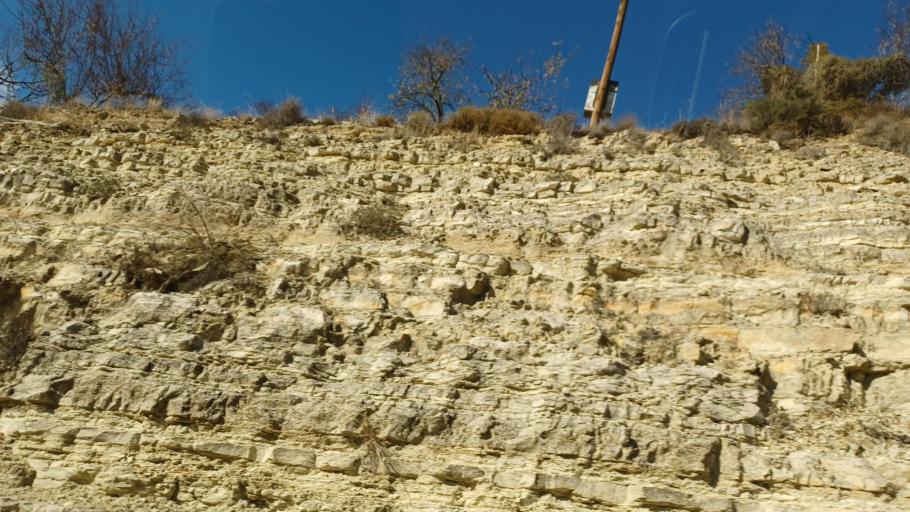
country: CY
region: Limassol
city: Pachna
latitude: 34.8237
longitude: 32.7993
